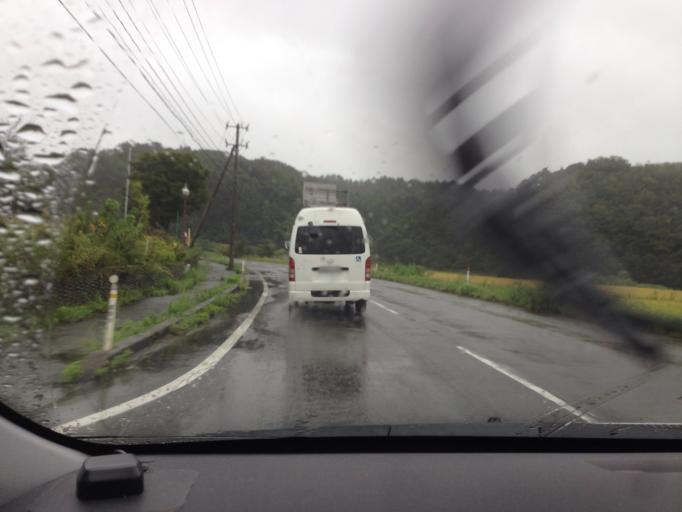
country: JP
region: Fukushima
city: Koriyama
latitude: 37.4182
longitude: 140.2760
